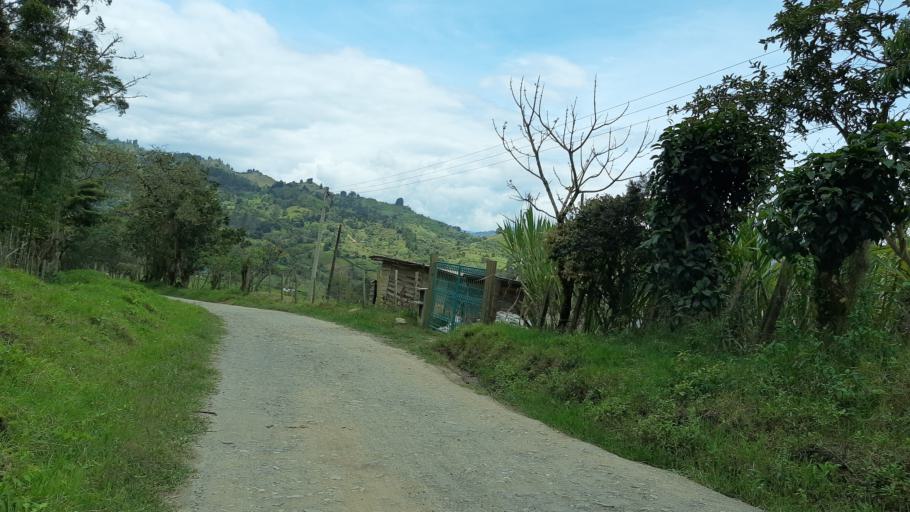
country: CO
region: Boyaca
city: Garagoa
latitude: 5.0714
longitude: -73.3618
